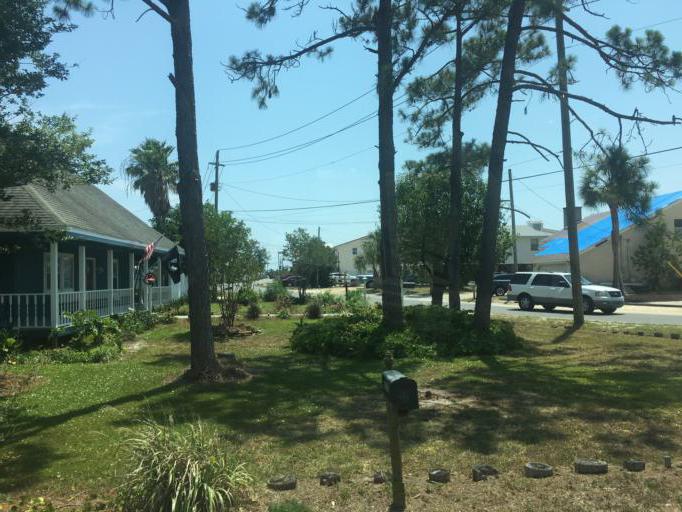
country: US
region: Florida
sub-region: Bay County
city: Lower Grand Lagoon
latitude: 30.1567
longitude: -85.7695
